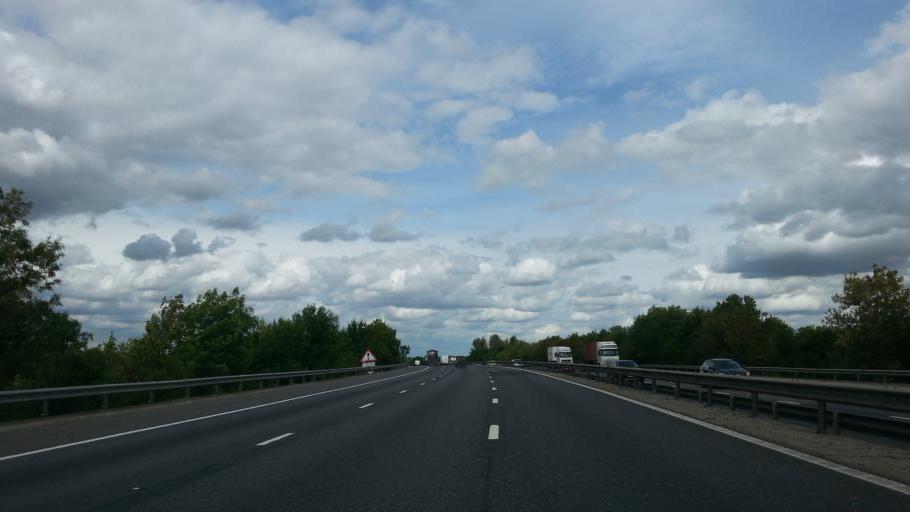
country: GB
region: England
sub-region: Essex
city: Little Hallingbury
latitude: 51.8170
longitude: 0.1844
